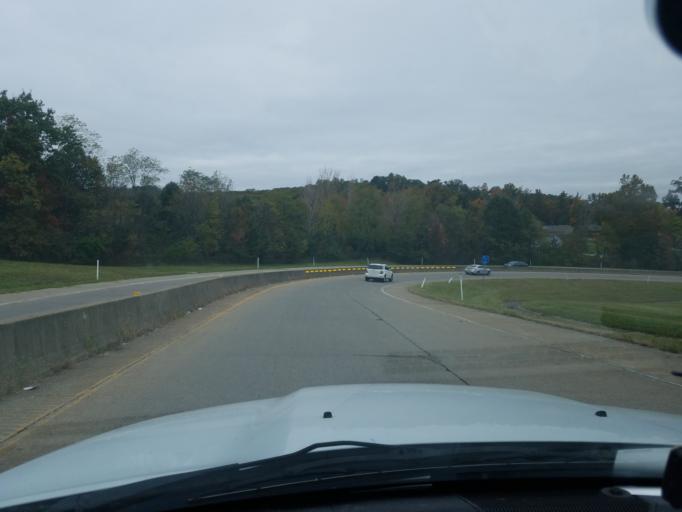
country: US
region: Indiana
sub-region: Floyd County
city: New Albany
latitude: 38.3133
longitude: -85.8454
